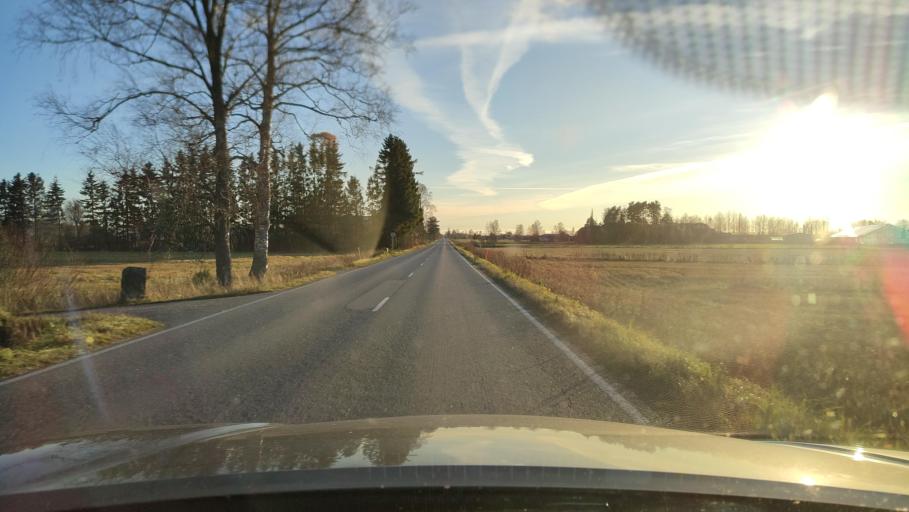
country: FI
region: Ostrobothnia
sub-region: Sydosterbotten
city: Naerpes
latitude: 62.6396
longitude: 21.5013
